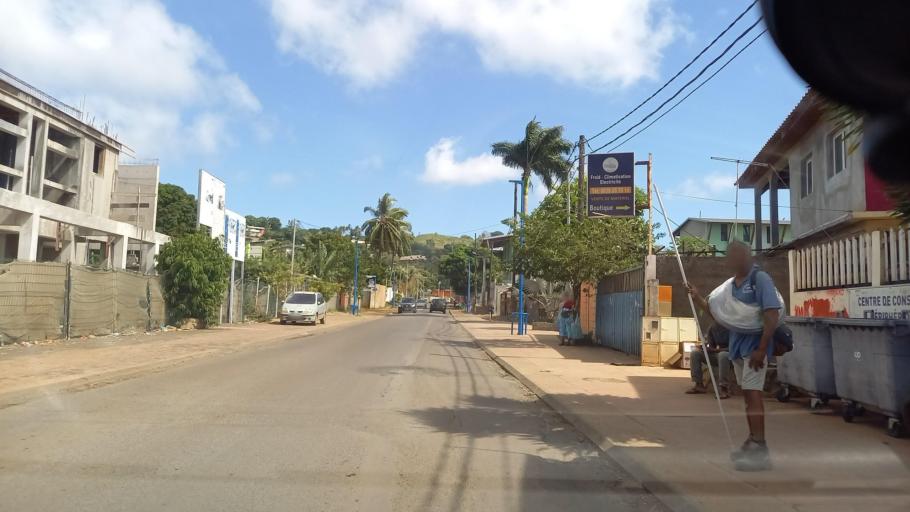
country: YT
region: Mamoudzou
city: Mamoudzou
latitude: -12.8010
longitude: 45.2085
